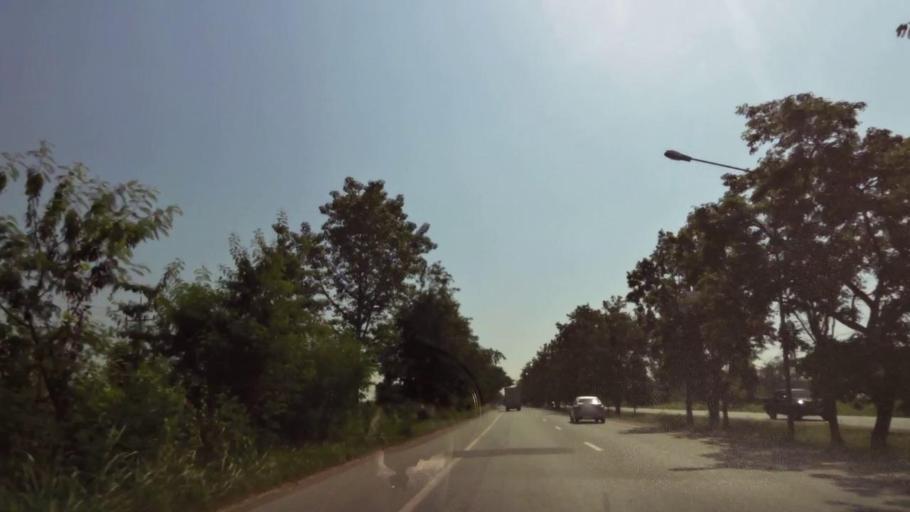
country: TH
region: Nakhon Sawan
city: Kao Liao
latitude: 15.9089
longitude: 100.1124
